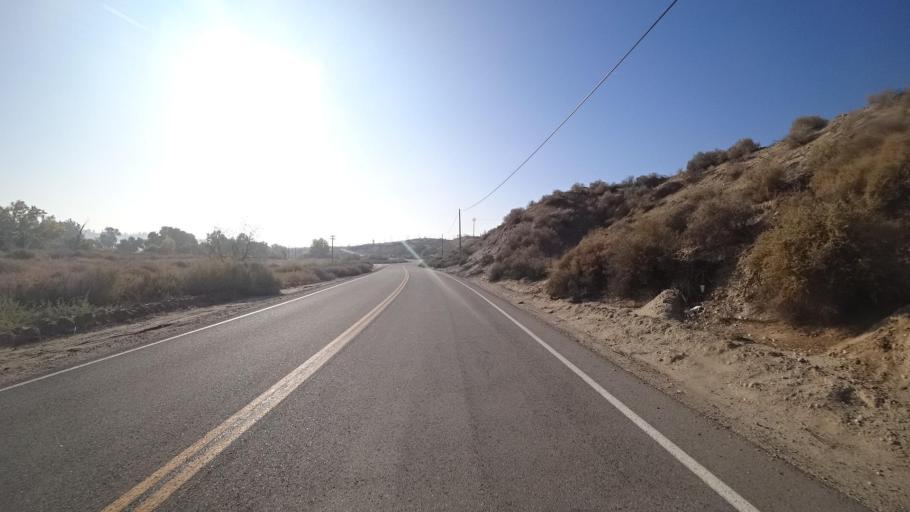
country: US
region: California
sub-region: Kern County
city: Oildale
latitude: 35.4351
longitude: -118.9486
